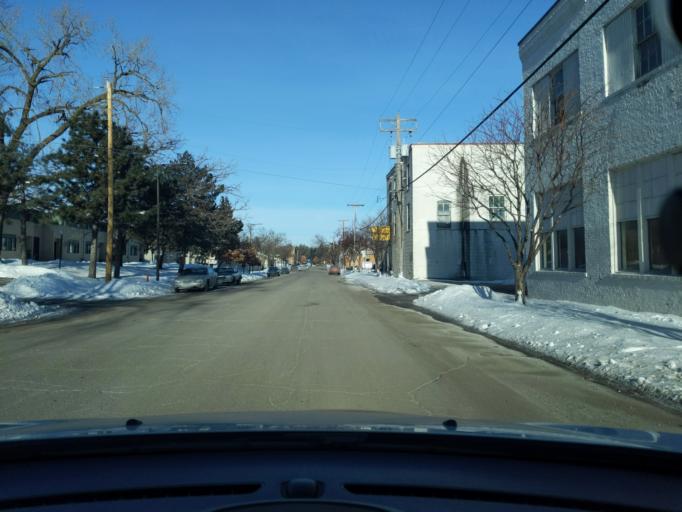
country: US
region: Minnesota
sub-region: Ramsey County
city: Lauderdale
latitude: 44.9675
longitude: -93.1944
